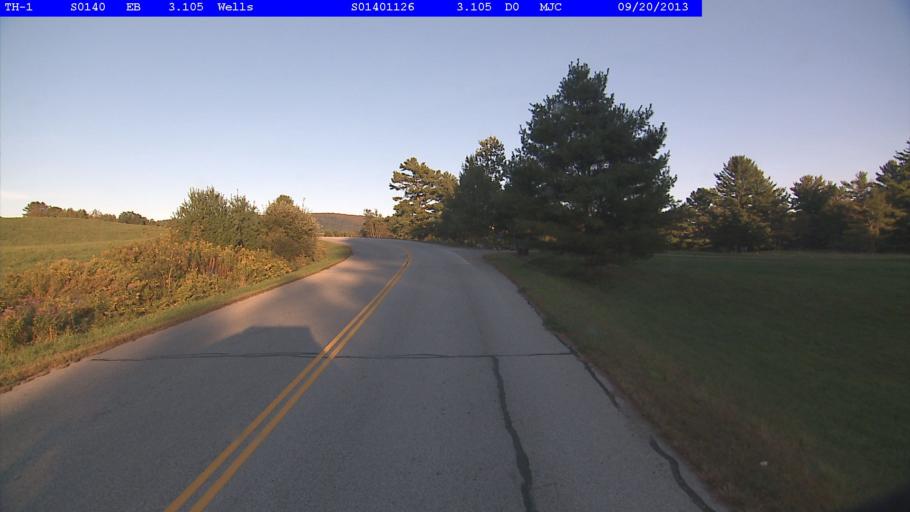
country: US
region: New York
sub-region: Washington County
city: Granville
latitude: 43.4110
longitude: -73.1469
